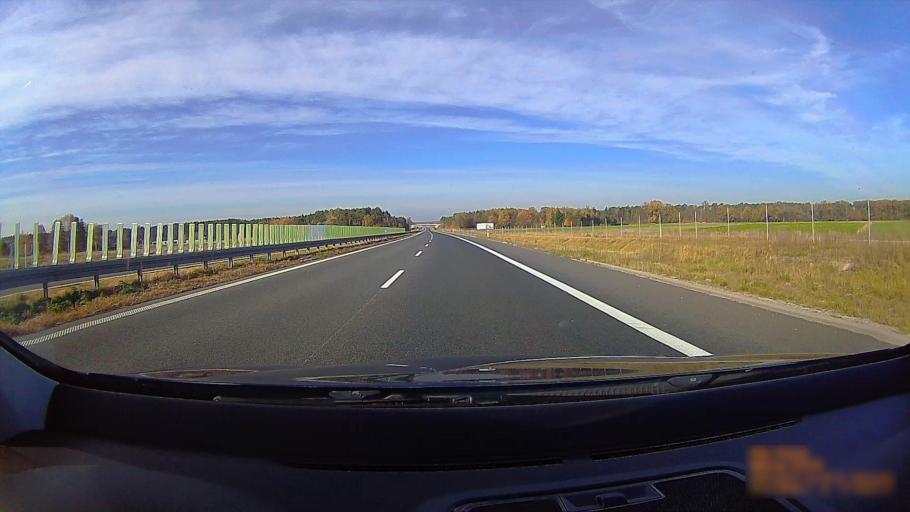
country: PL
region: Greater Poland Voivodeship
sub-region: Powiat ostrowski
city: Ostrow Wielkopolski
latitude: 51.6469
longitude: 17.8740
